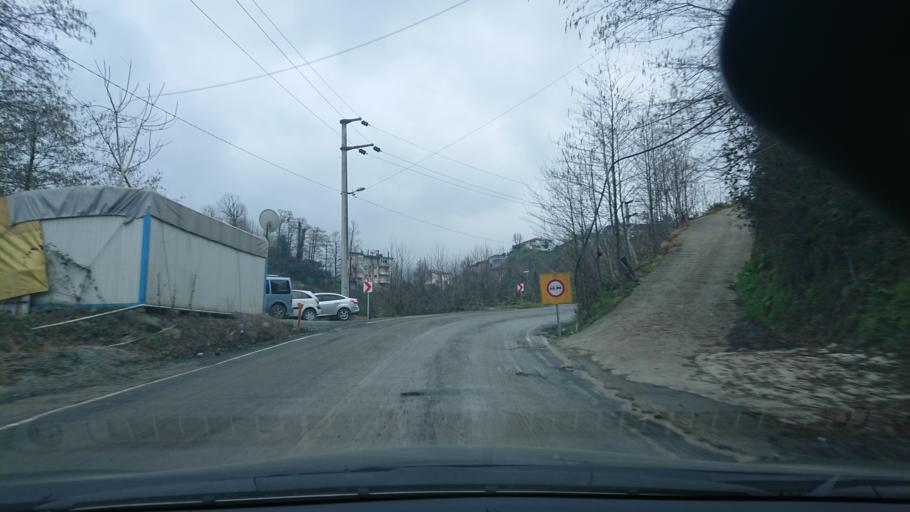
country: TR
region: Rize
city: Rize
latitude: 41.0178
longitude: 40.4988
